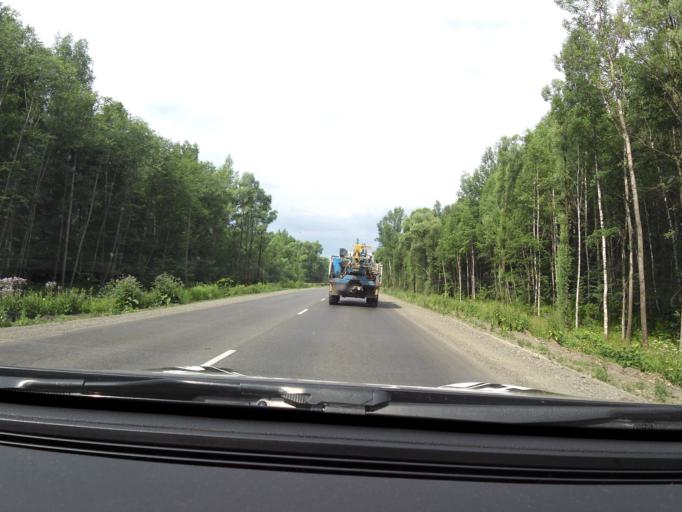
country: RU
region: Chelyabinsk
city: Asha
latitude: 54.8814
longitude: 57.2491
